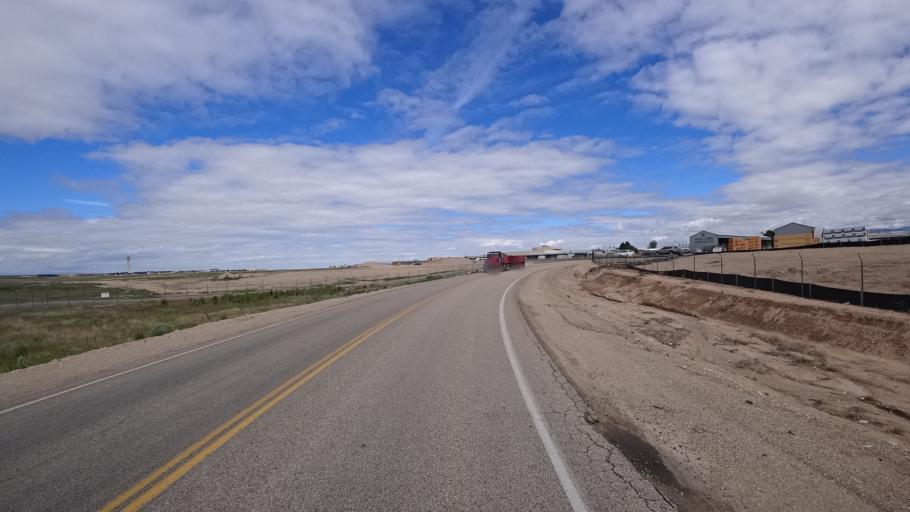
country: US
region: Idaho
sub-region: Ada County
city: Boise
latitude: 43.5565
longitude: -116.1931
